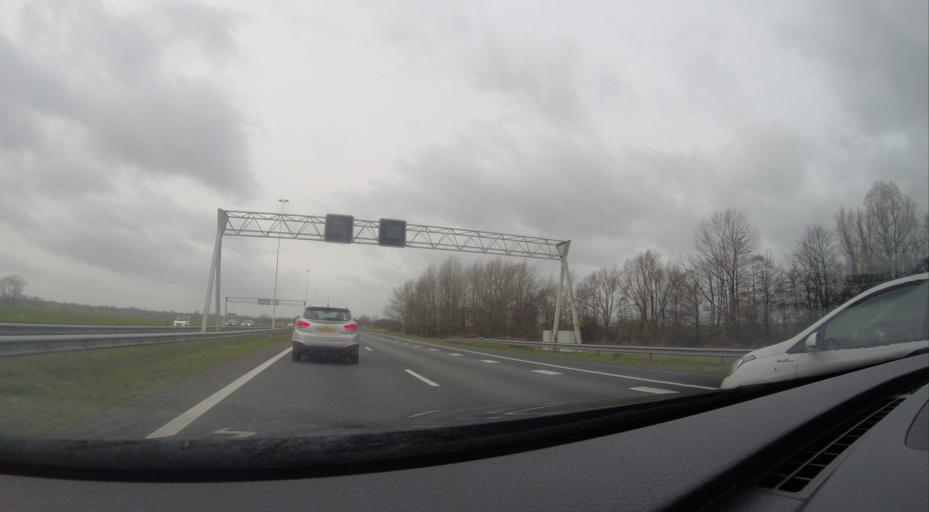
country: NL
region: Utrecht
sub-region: Gemeente Baarn
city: Baarn
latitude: 52.2150
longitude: 5.3274
